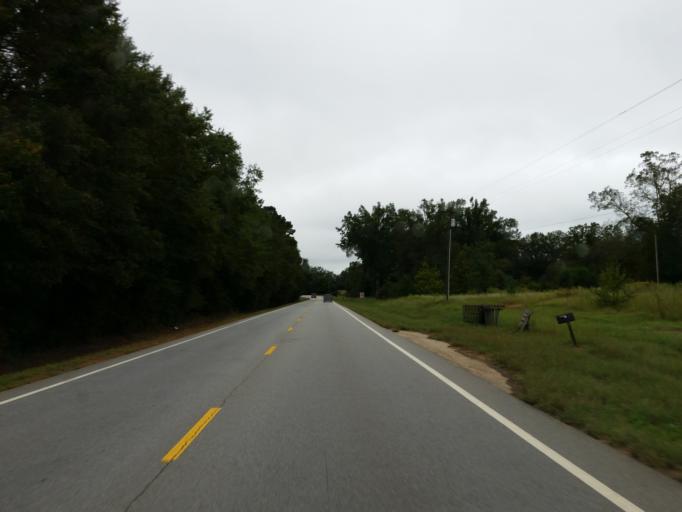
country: US
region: Georgia
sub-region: Lamar County
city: Barnesville
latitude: 32.9973
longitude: -84.1213
